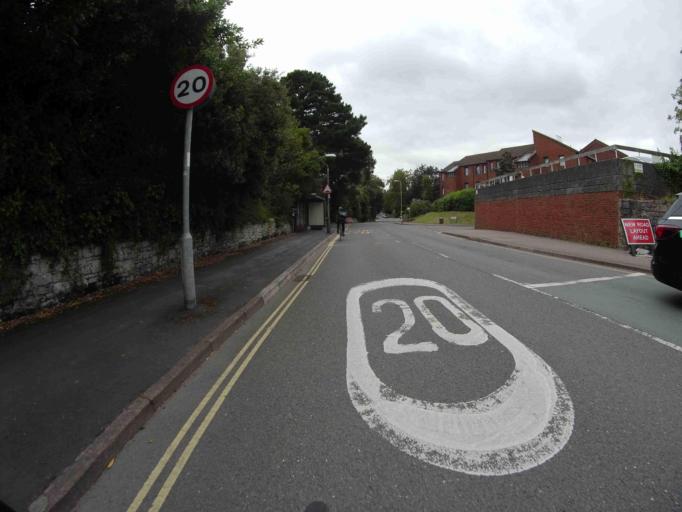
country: GB
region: England
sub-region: Devon
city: Heavitree
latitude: 50.7155
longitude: -3.5105
